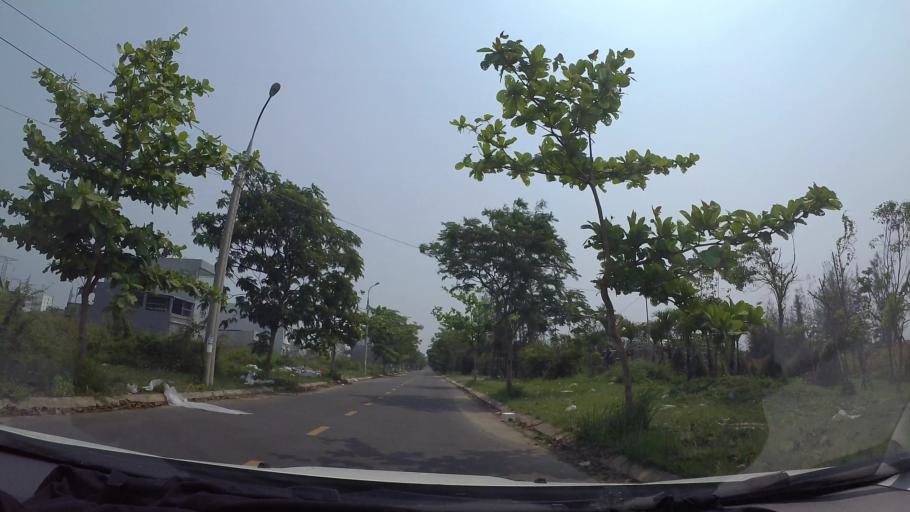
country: VN
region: Da Nang
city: Cam Le
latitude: 15.9978
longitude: 108.2082
